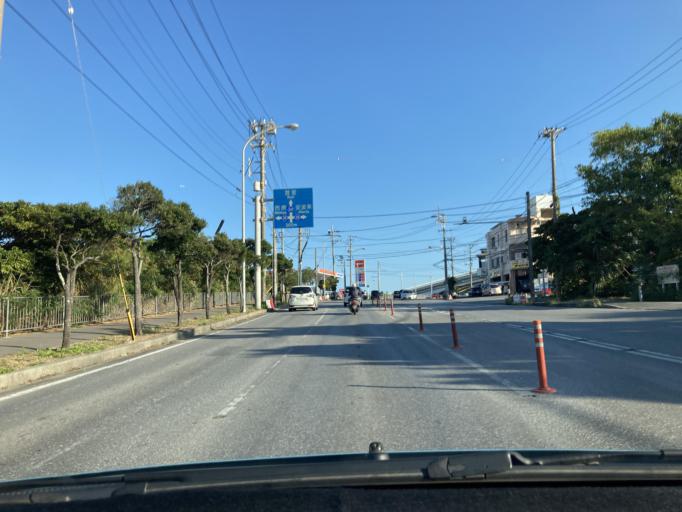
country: JP
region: Okinawa
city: Ginowan
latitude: 26.2435
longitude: 127.7390
